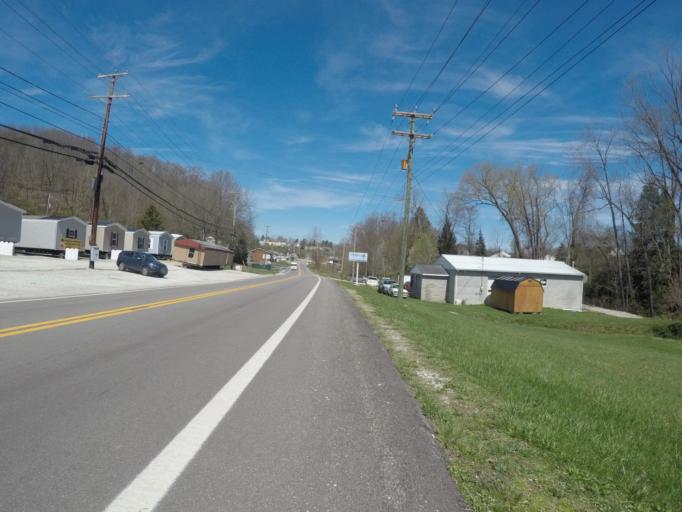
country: US
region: West Virginia
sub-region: Cabell County
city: Pea Ridge
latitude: 38.4047
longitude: -82.3198
